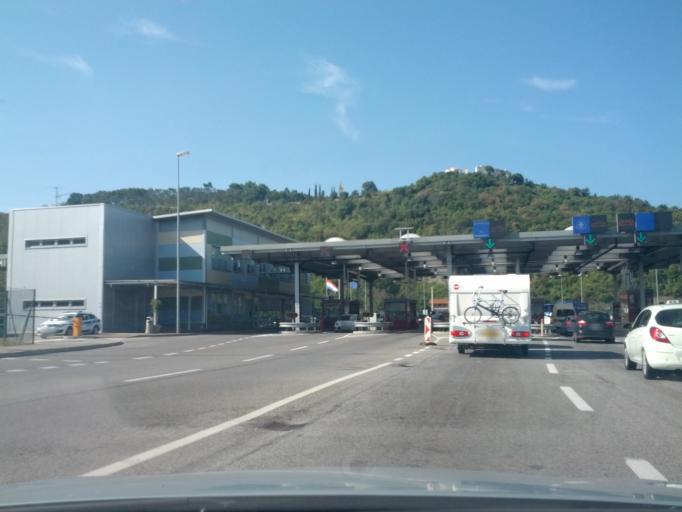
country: HR
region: Istarska
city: Buje
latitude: 45.4553
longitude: 13.6571
